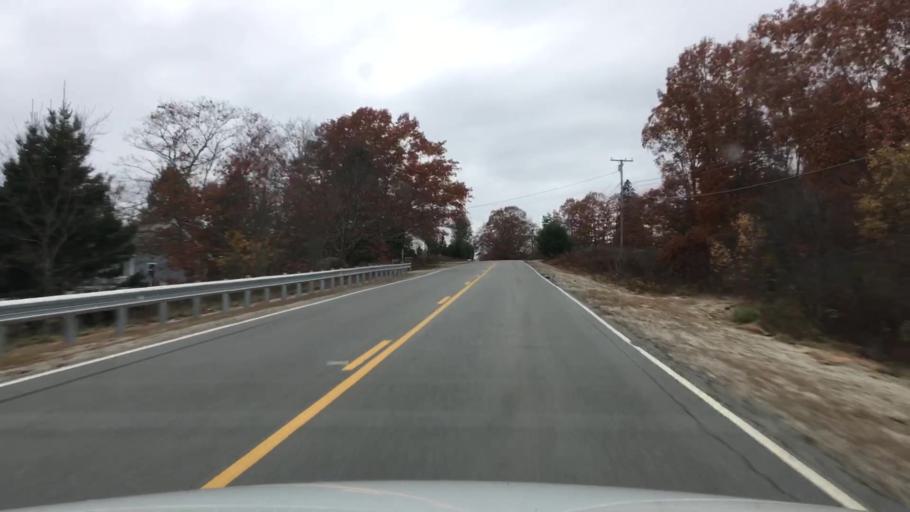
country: US
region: Maine
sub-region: Hancock County
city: Sedgwick
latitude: 44.3901
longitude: -68.5794
